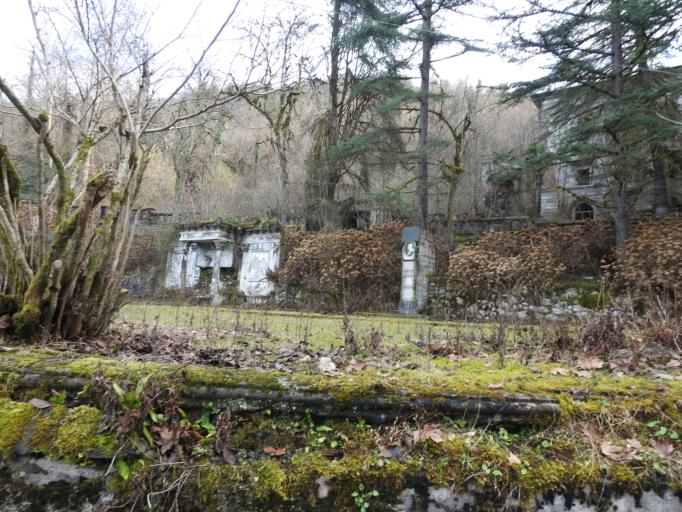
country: GE
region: Abkhazia
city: Tqvarch'eli
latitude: 42.8585
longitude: 41.7759
